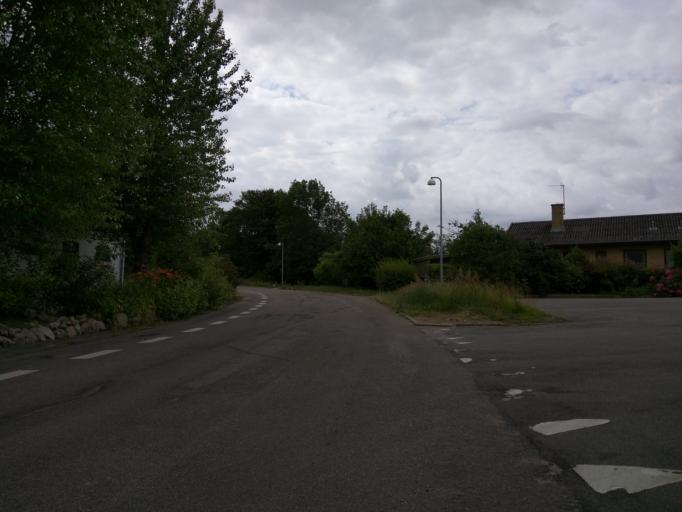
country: DK
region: Zealand
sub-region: Kalundborg Kommune
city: Svebolle
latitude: 55.7128
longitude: 11.3016
